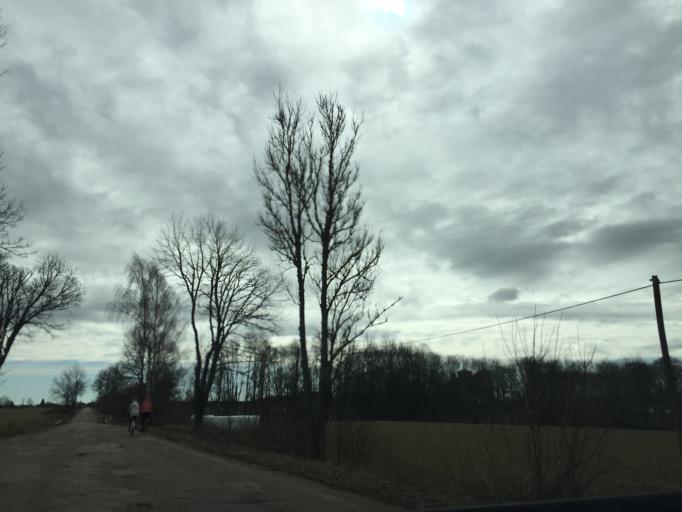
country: LV
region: Daugavpils
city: Daugavpils
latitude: 55.9295
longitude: 26.7206
